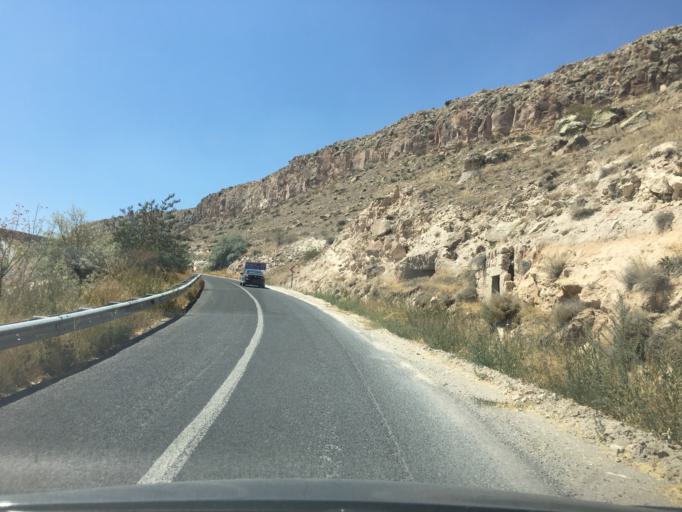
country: TR
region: Nevsehir
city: Urgub
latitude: 38.4695
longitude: 34.9419
